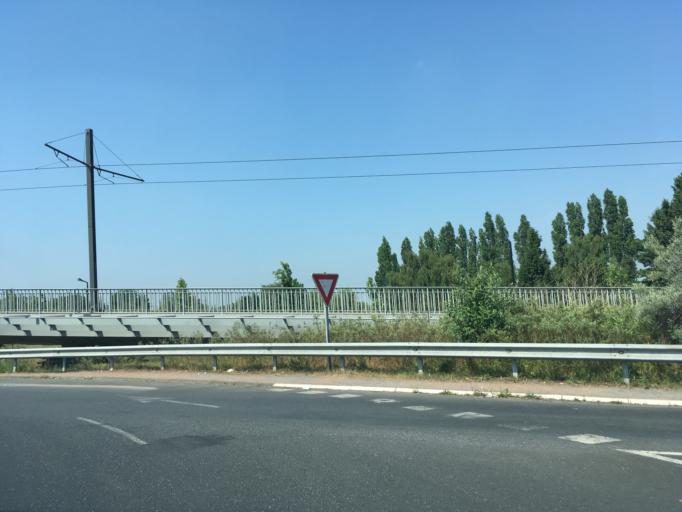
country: FR
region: Nord-Pas-de-Calais
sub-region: Departement du Nord
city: Valenciennes
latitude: 50.3443
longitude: 3.5170
